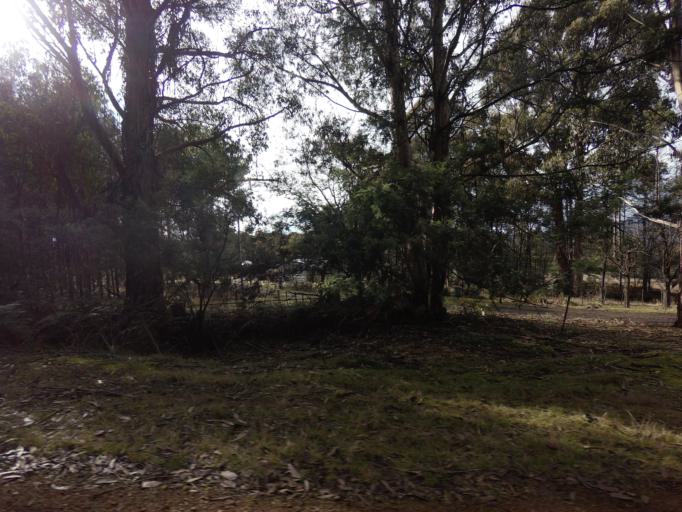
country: AU
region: Tasmania
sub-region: Derwent Valley
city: New Norfolk
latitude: -42.7870
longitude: 146.9174
